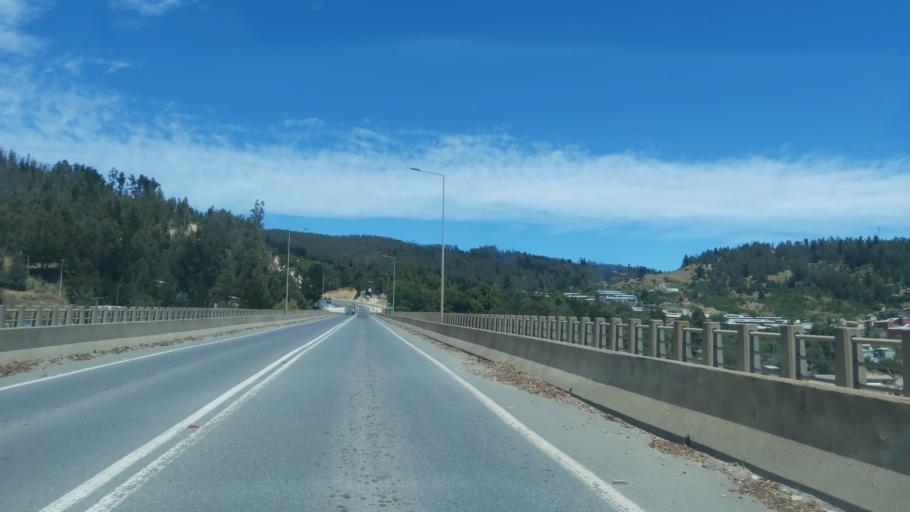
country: CL
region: Maule
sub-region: Provincia de Talca
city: Constitucion
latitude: -35.3418
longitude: -72.3936
